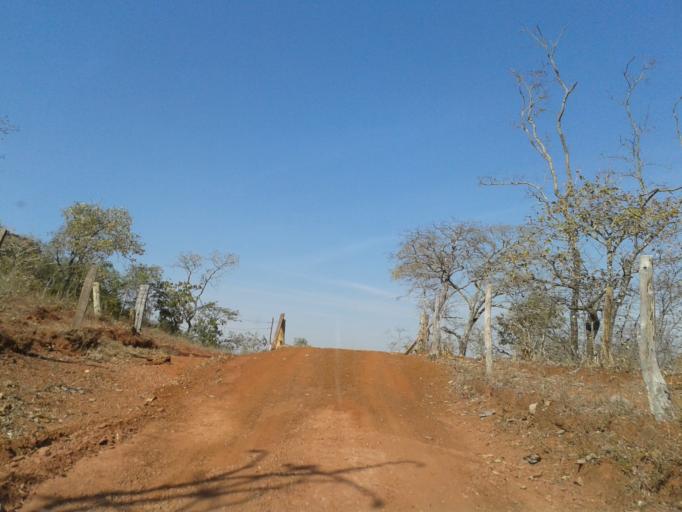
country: BR
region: Minas Gerais
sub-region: Santa Vitoria
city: Santa Vitoria
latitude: -19.2291
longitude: -50.0410
